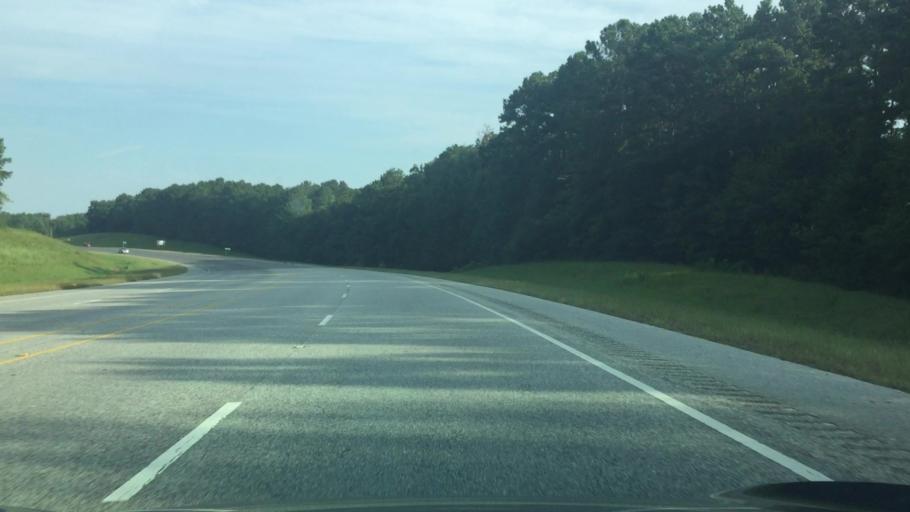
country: US
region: Alabama
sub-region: Butler County
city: Georgiana
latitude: 31.5131
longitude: -86.7021
